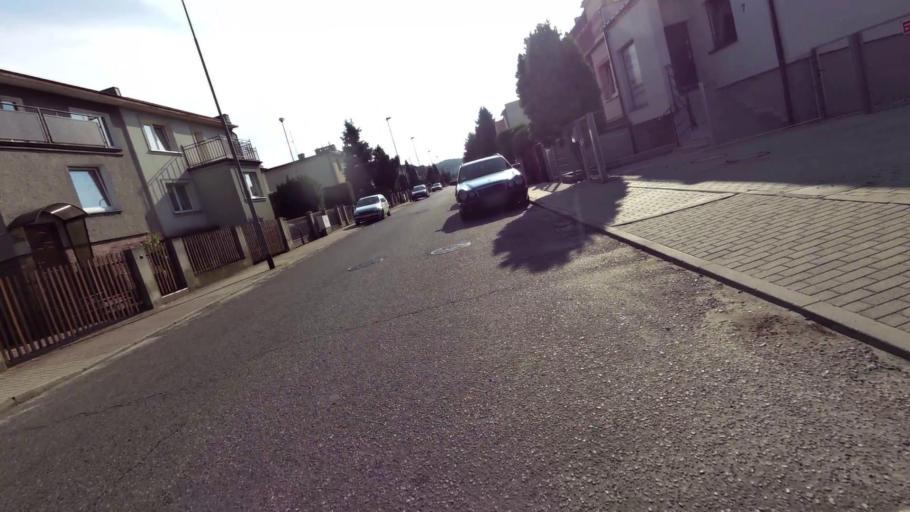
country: PL
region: West Pomeranian Voivodeship
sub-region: Szczecin
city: Szczecin
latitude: 53.3841
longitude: 14.6443
